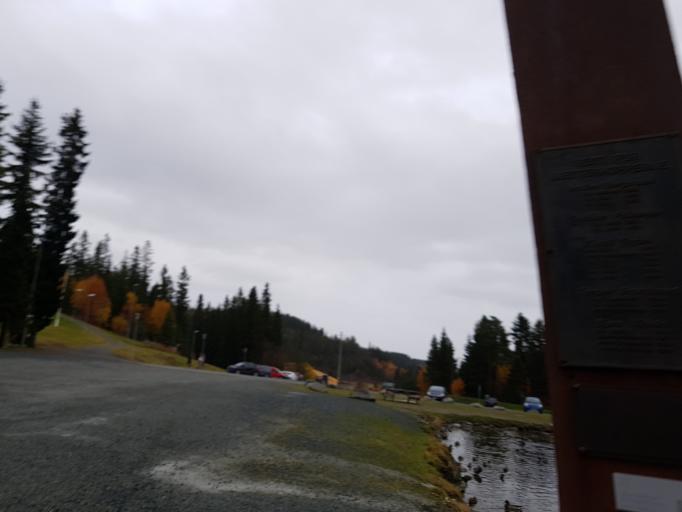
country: NO
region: Sor-Trondelag
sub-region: Melhus
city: Melhus
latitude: 63.3778
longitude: 10.3107
